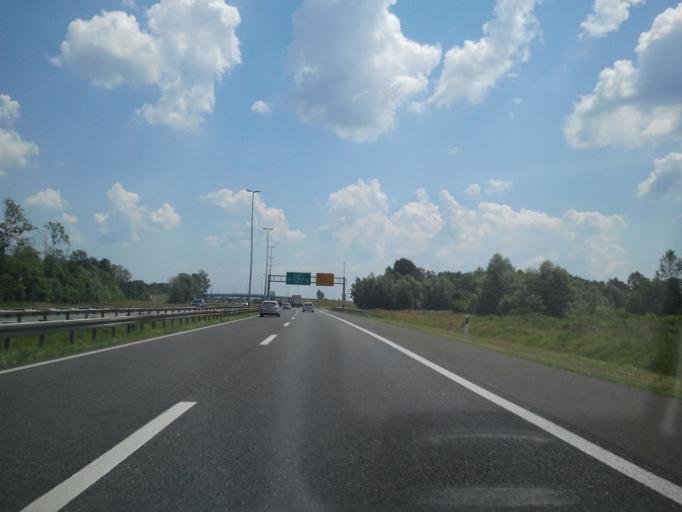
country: HR
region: Zagrebacka
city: Lupoglav
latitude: 45.6879
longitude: 16.3817
